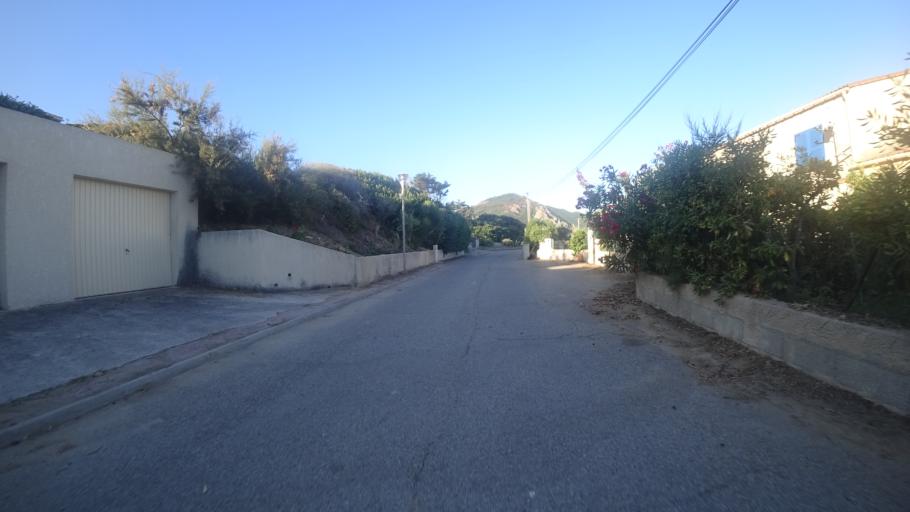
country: FR
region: Corsica
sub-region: Departement de la Corse-du-Sud
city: Alata
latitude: 41.9805
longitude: 8.6677
